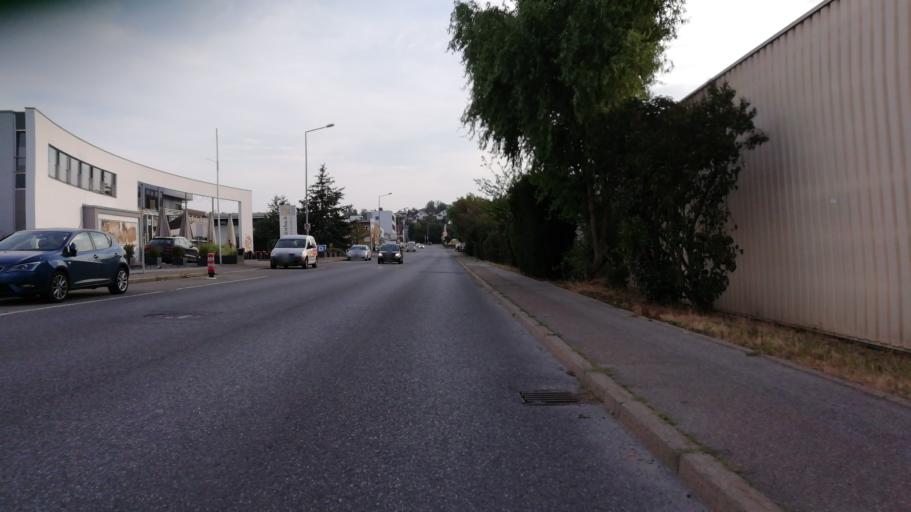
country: DE
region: Baden-Wuerttemberg
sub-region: Regierungsbezirk Stuttgart
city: Weil der Stadt
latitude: 48.7573
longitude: 8.8715
